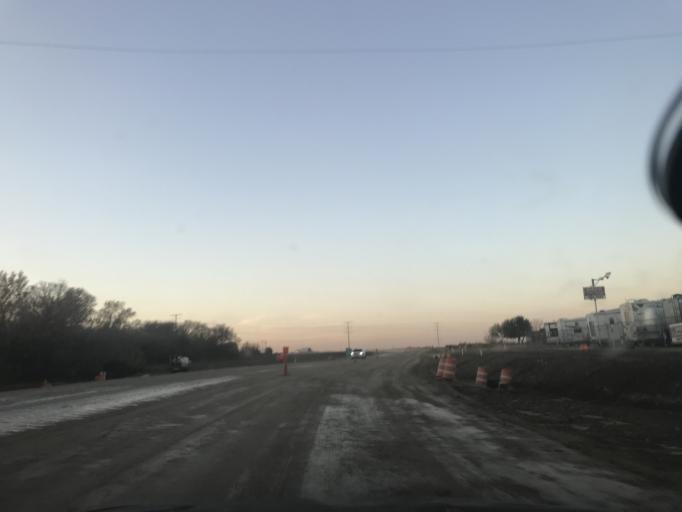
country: US
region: Texas
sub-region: Williamson County
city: Hutto
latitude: 30.5065
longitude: -97.5213
